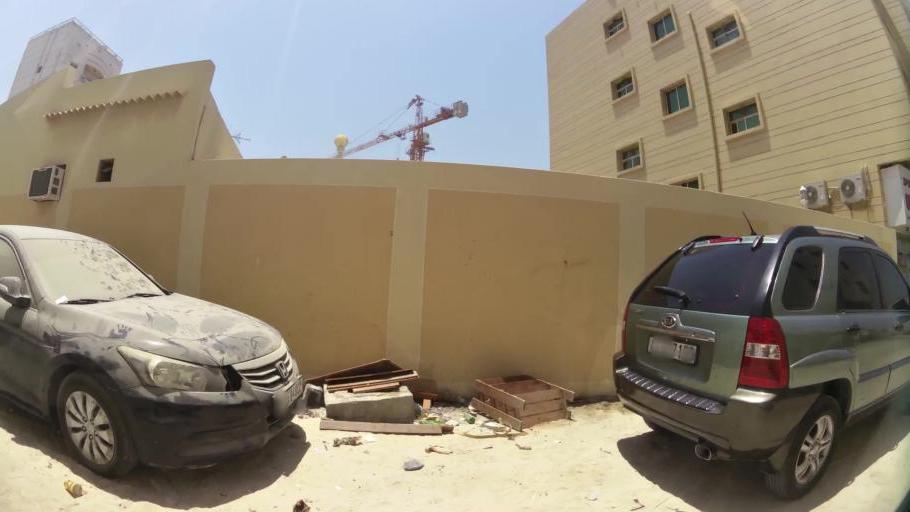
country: AE
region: Ajman
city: Ajman
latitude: 25.4043
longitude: 55.4371
